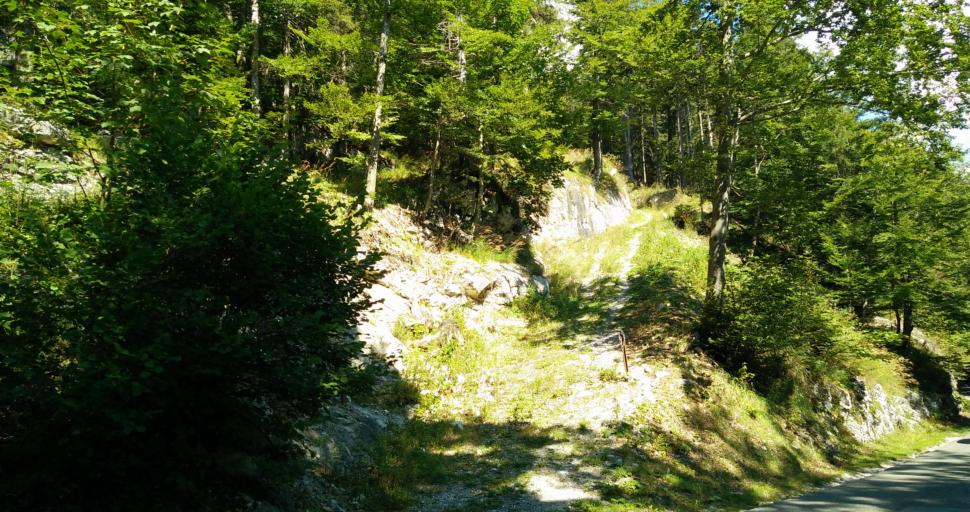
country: AT
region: Salzburg
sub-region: Politischer Bezirk Hallein
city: Scheffau am Tennengebirge
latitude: 47.6306
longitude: 13.2361
